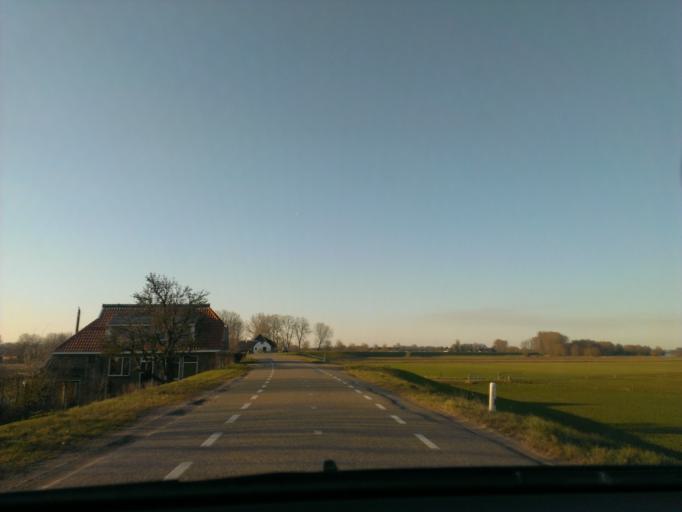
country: NL
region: Overijssel
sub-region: Gemeente Olst-Wijhe
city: Olst
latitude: 52.3132
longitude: 6.0895
